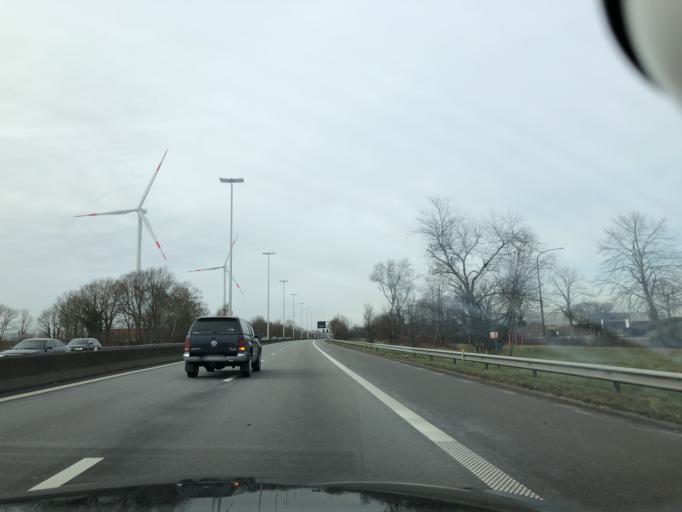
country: BE
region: Flanders
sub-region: Provincie Antwerpen
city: Geel
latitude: 51.1209
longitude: 4.9644
